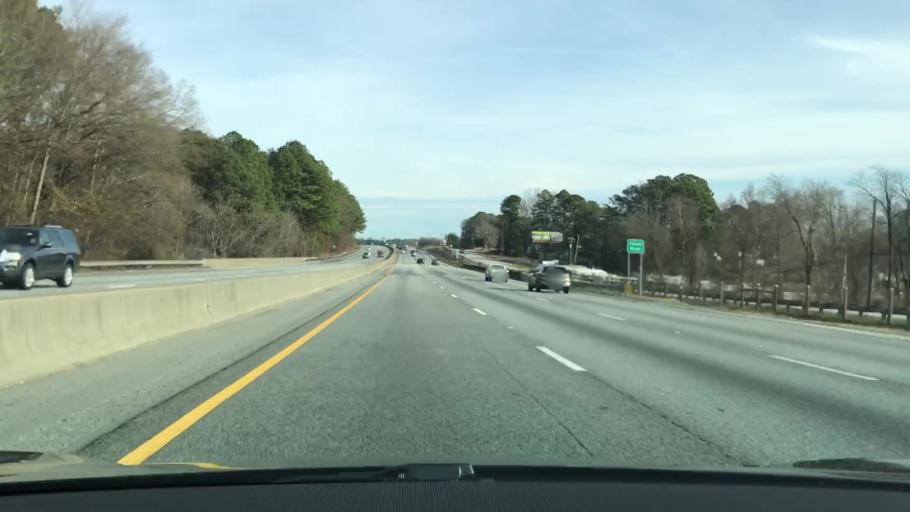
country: US
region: Georgia
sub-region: Newton County
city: Porterdale
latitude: 33.6149
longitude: -83.9163
